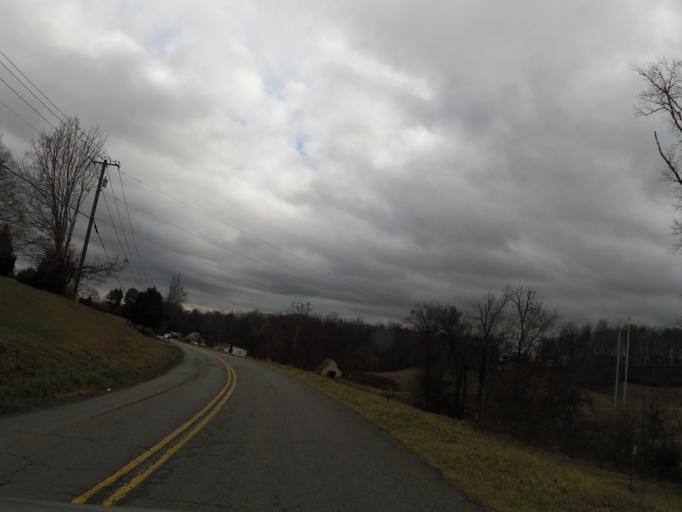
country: US
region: Tennessee
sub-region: Grainger County
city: Blaine
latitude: 36.1443
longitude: -83.6859
